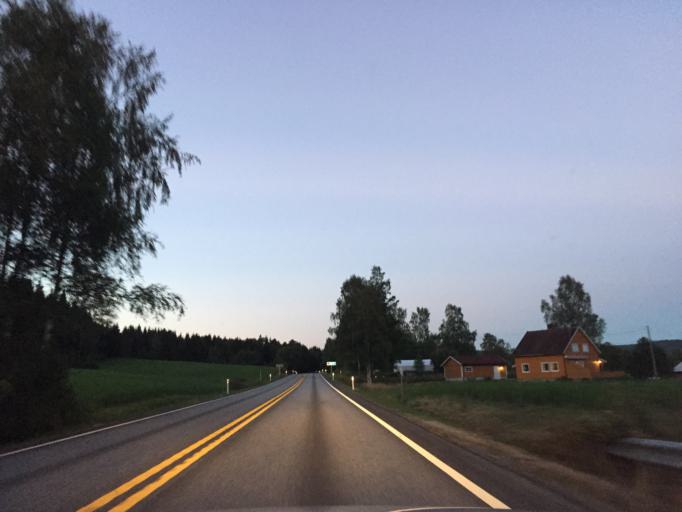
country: NO
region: Hedmark
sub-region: Kongsvinger
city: Spetalen
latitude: 60.2110
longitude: 11.9102
